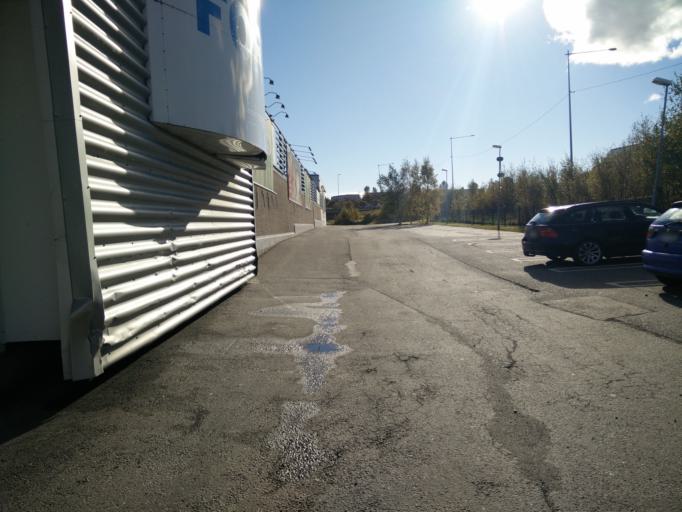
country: SE
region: Vaesternorrland
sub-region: Haernoesands Kommun
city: Haernoesand
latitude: 62.6355
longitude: 17.9244
